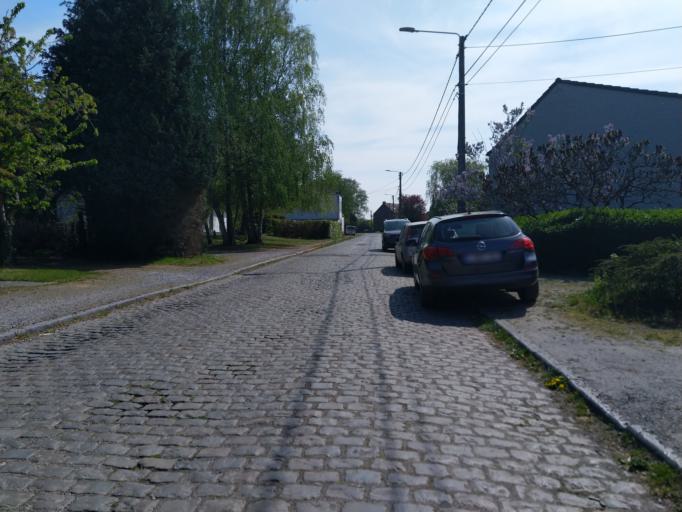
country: BE
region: Wallonia
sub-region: Province du Hainaut
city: Mons
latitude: 50.4570
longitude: 4.0343
